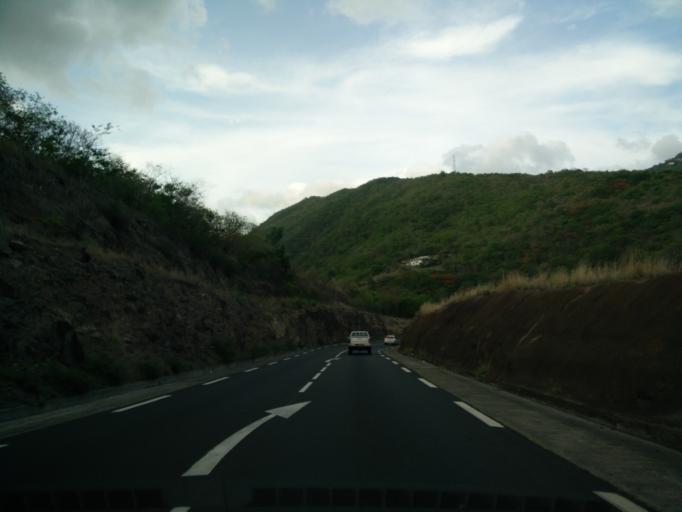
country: MQ
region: Martinique
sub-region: Martinique
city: Saint-Pierre
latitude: 14.6801
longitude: -61.1667
